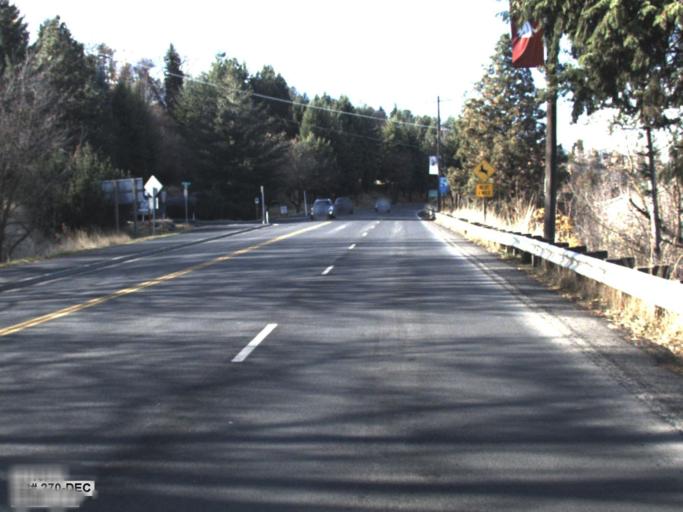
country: US
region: Washington
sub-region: Whitman County
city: Pullman
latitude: 46.7321
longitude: -117.1828
